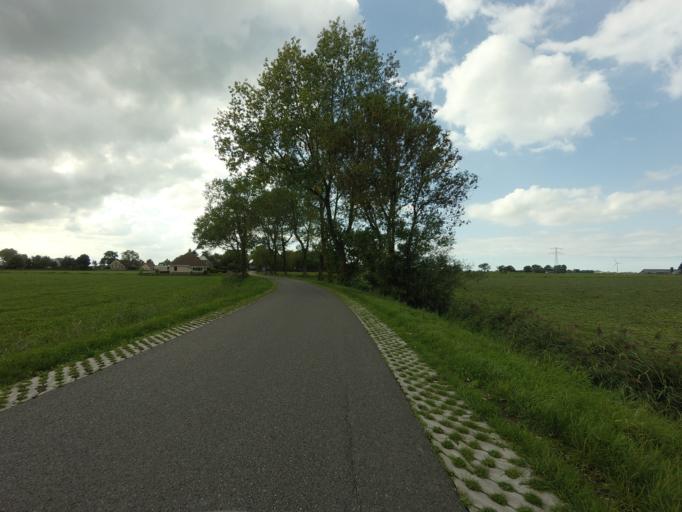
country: NL
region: Friesland
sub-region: Sudwest Fryslan
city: Bolsward
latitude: 53.0684
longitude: 5.5722
